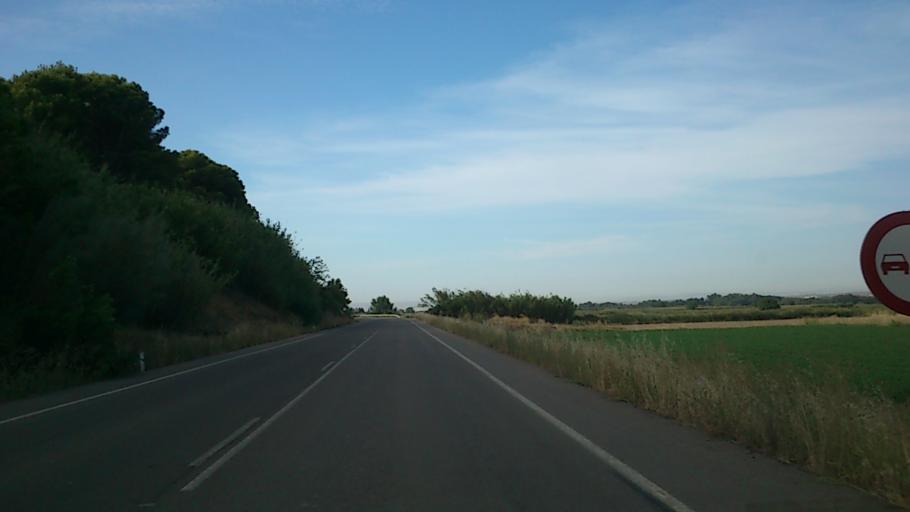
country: ES
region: Aragon
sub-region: Provincia de Zaragoza
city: Villanueva de Gallego
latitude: 41.7865
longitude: -0.7860
